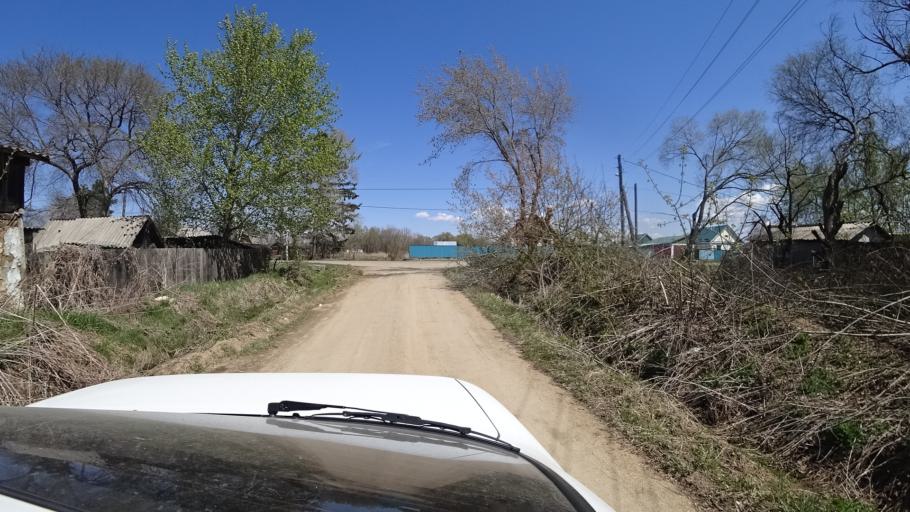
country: RU
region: Primorskiy
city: Dal'nerechensk
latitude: 45.7950
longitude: 133.7708
